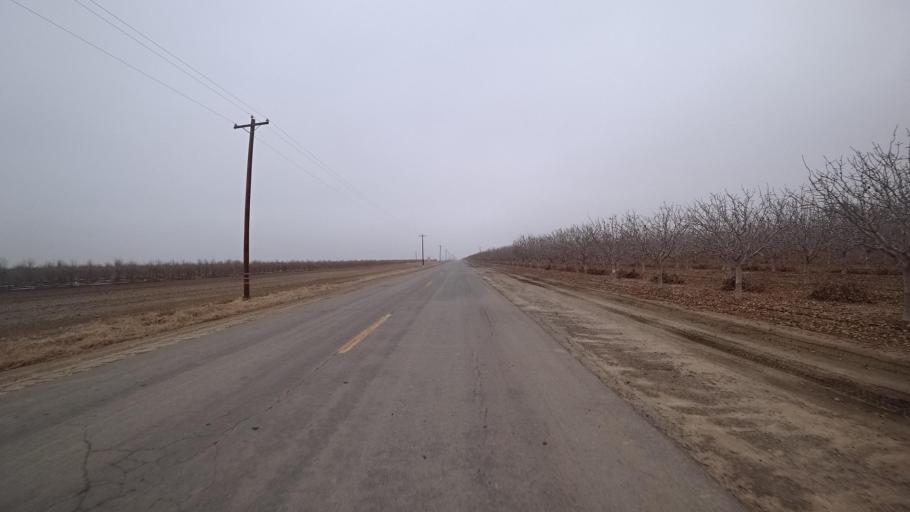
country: US
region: California
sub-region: Kern County
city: Wasco
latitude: 35.6419
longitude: -119.5088
